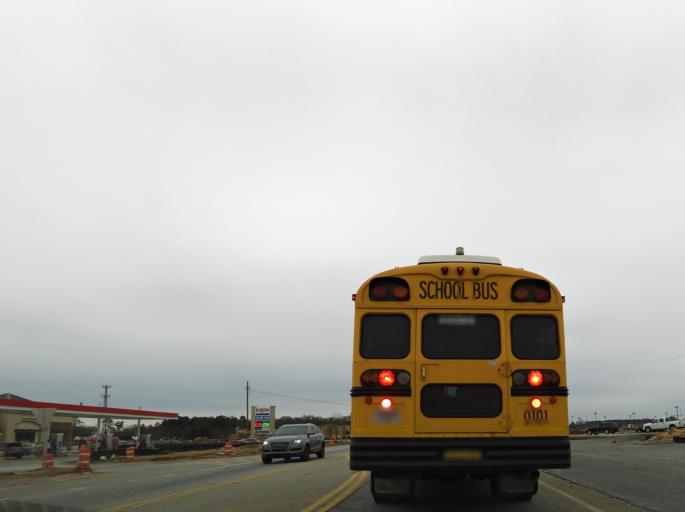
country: US
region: Georgia
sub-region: Houston County
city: Centerville
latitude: 32.5510
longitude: -83.6905
